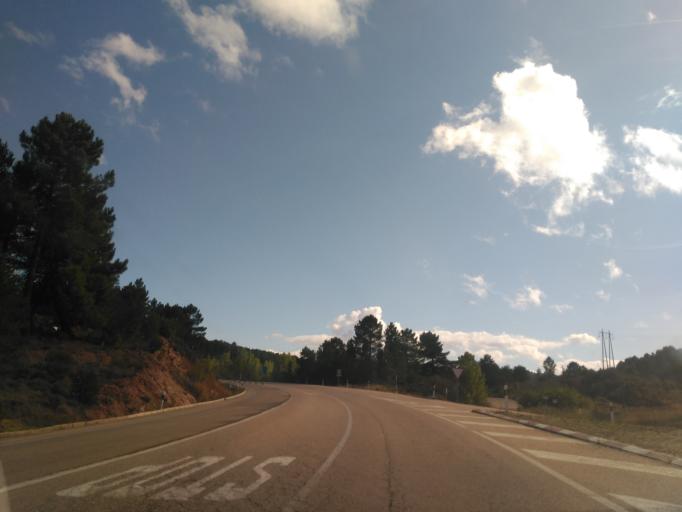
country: ES
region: Castille and Leon
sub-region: Provincia de Burgos
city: Pinilla de los Barruecos
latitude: 41.9068
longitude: -3.2766
